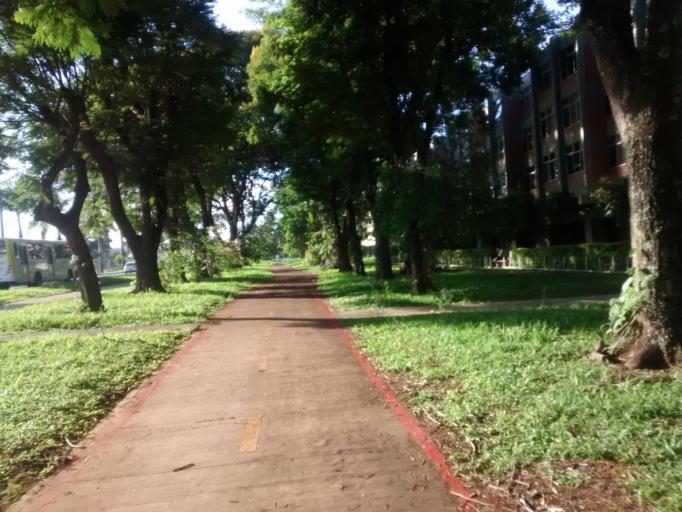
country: BR
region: Federal District
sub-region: Brasilia
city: Brasilia
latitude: -15.7553
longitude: -47.8797
